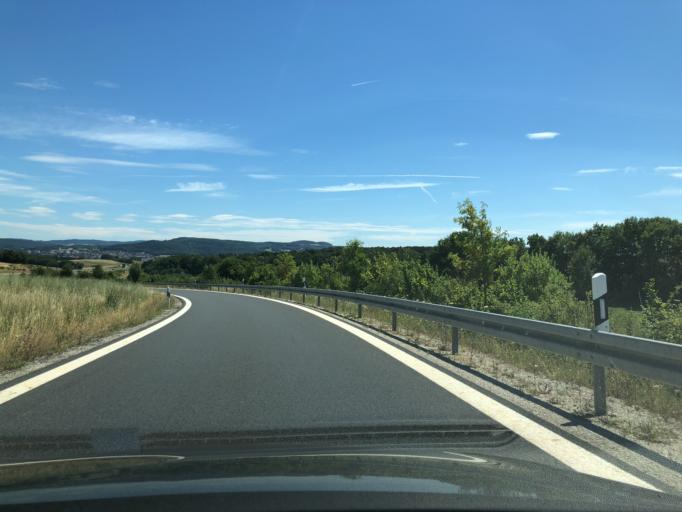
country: DE
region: Bavaria
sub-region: Upper Franconia
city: Untersiemau
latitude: 50.1632
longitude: 11.0078
